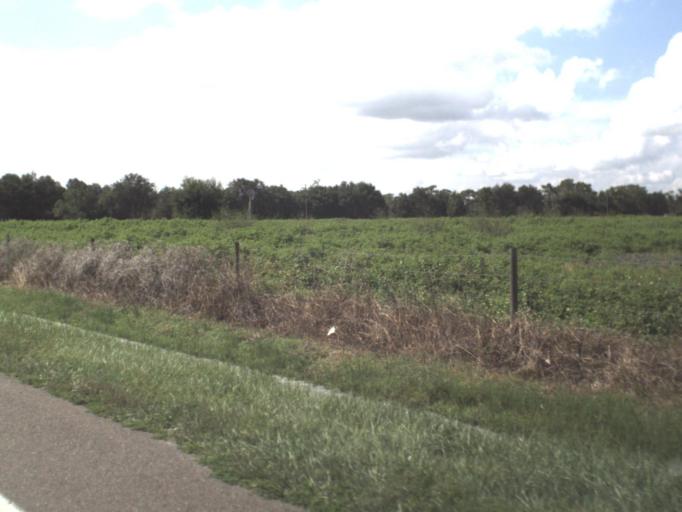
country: US
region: Florida
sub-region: Hardee County
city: Zolfo Springs
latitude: 27.4822
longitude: -81.9104
